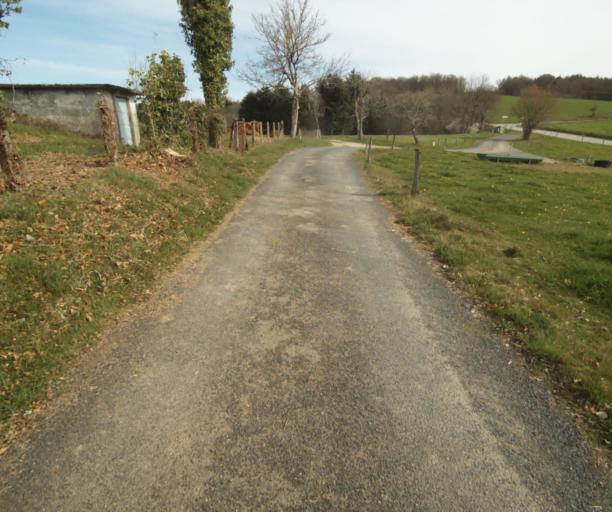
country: FR
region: Limousin
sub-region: Departement de la Correze
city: Correze
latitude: 45.3916
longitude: 1.8232
